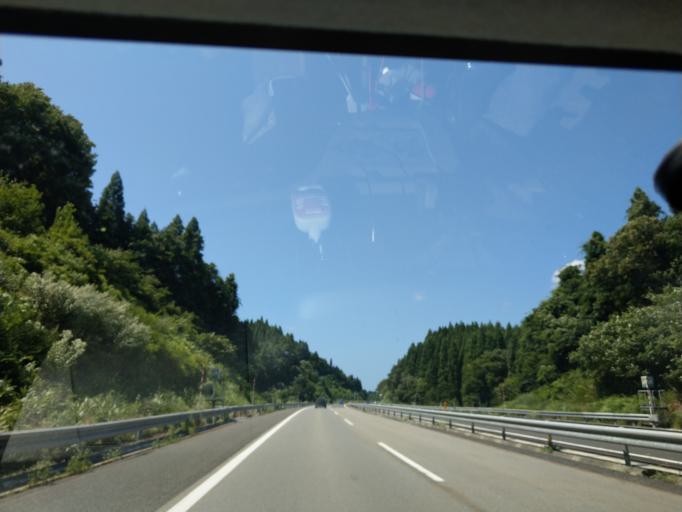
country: JP
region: Akita
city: Akita
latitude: 39.6237
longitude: 140.2386
